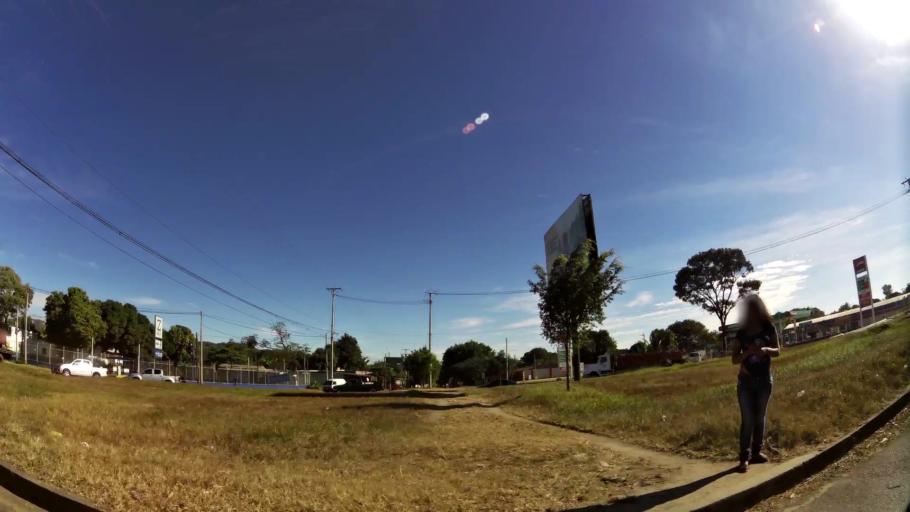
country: SV
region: Santa Ana
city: Santa Ana
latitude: 13.9733
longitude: -89.5859
